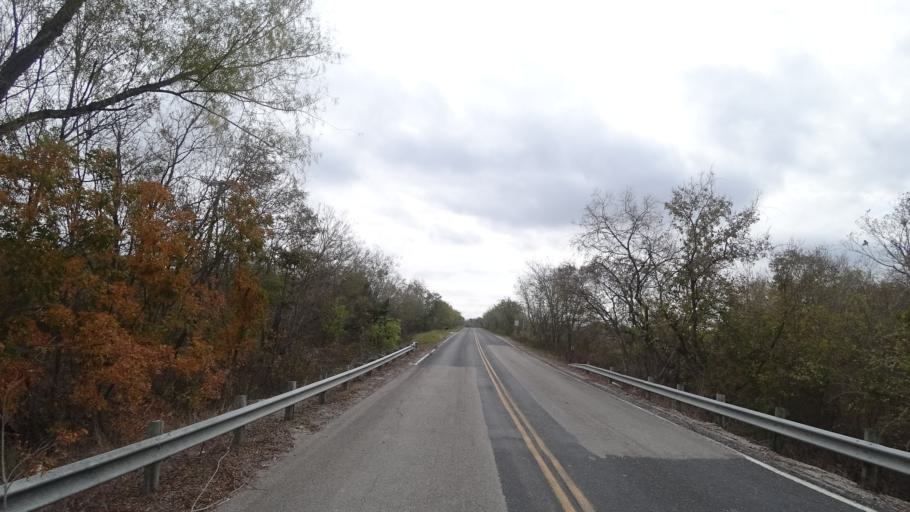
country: US
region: Texas
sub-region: Travis County
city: Pflugerville
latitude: 30.3952
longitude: -97.5893
